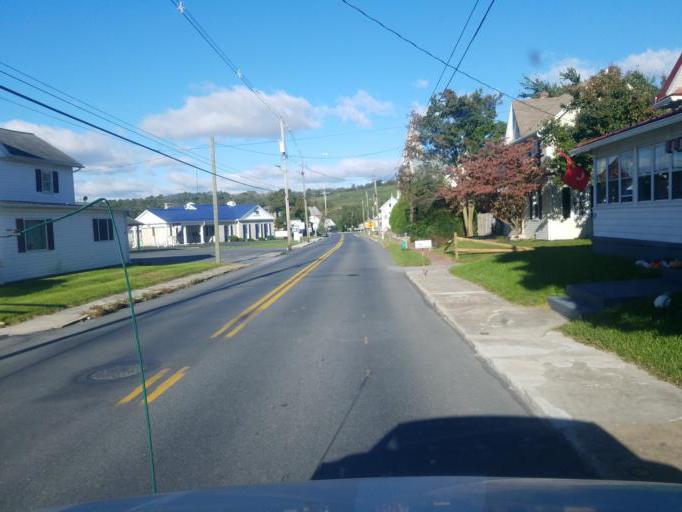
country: US
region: Pennsylvania
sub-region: Franklin County
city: Mont Alto
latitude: 39.8437
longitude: -77.5567
